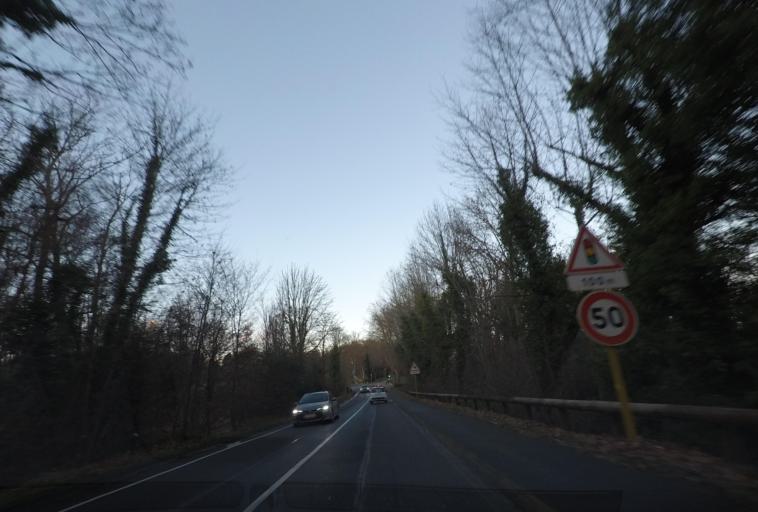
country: FR
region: Ile-de-France
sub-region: Departement de l'Essonne
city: Mennecy
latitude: 48.5774
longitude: 2.4343
